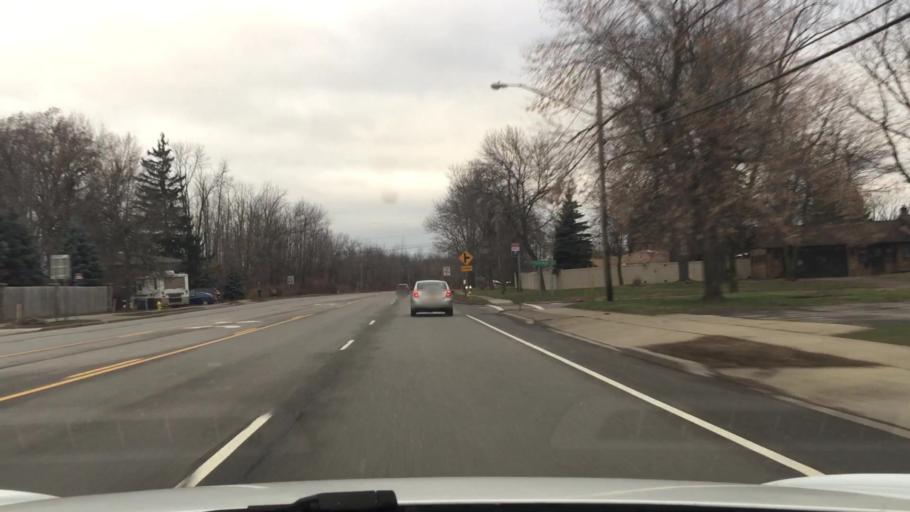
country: US
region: New York
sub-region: Erie County
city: Williamsville
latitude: 42.9784
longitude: -78.7576
